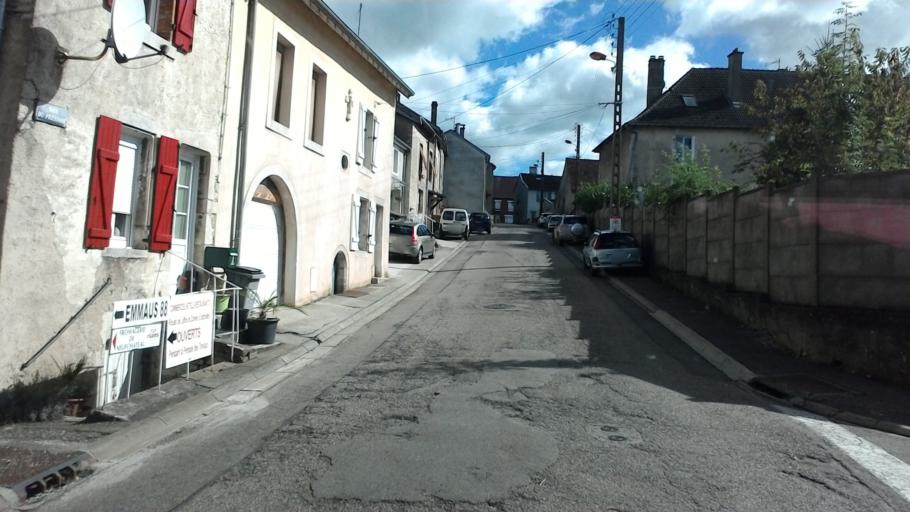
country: FR
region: Lorraine
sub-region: Departement des Vosges
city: Neufchateau
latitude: 48.3639
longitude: 5.6896
